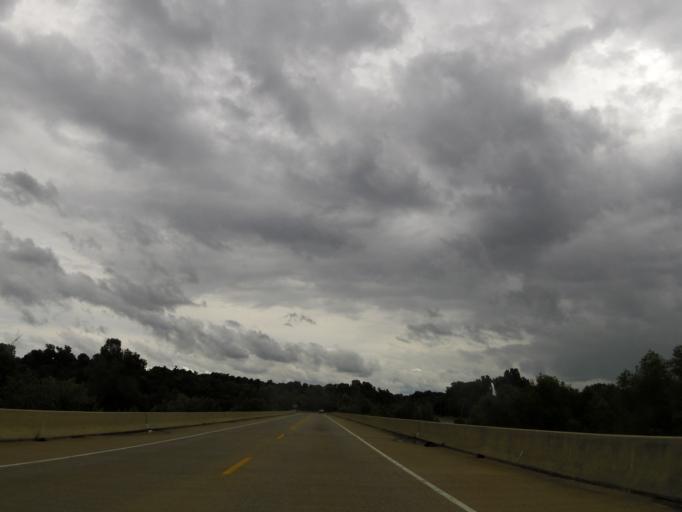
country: US
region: Kentucky
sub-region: Ballard County
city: Wickliffe
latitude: 36.9755
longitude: -89.0972
